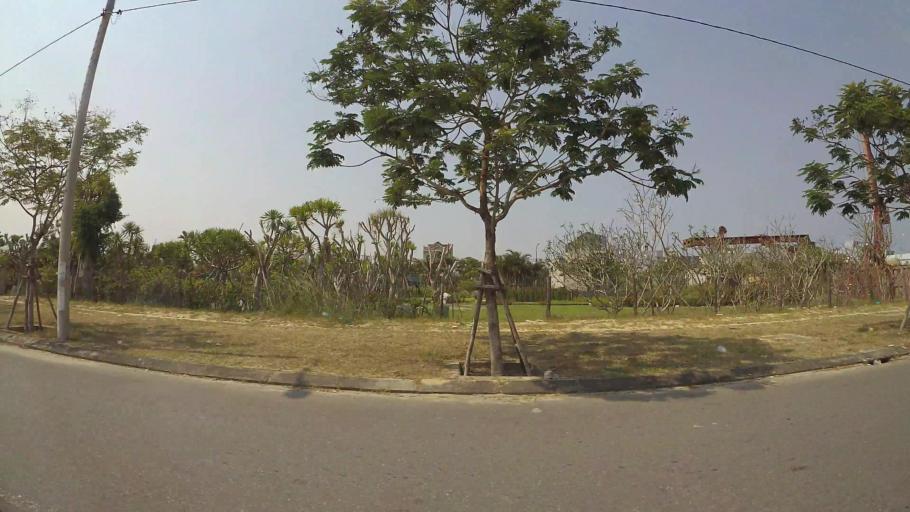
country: VN
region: Da Nang
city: Ngu Hanh Son
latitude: 15.9784
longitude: 108.2710
